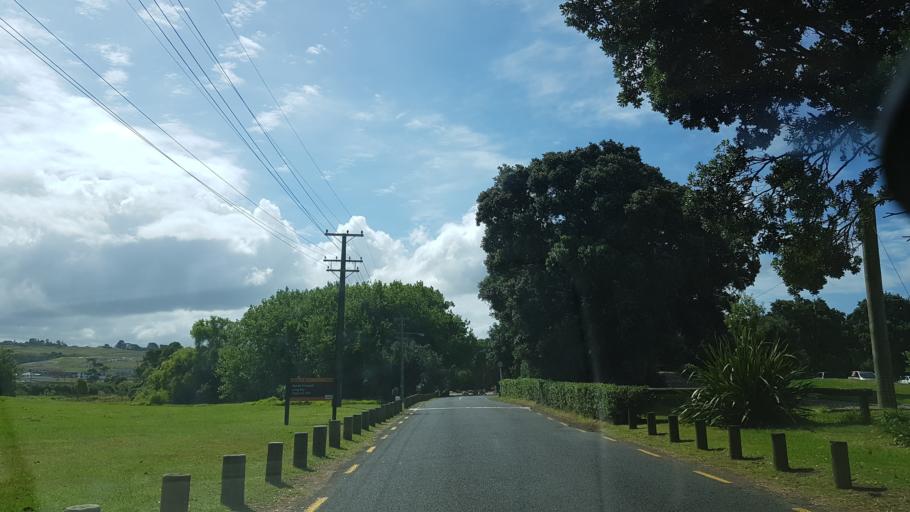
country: NZ
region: Auckland
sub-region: Auckland
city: Rothesay Bay
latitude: -36.6844
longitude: 174.7487
